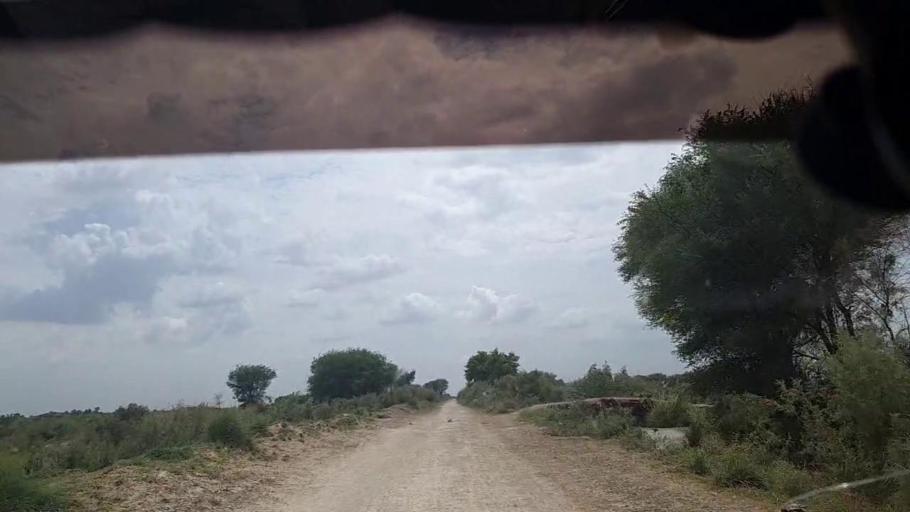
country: PK
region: Sindh
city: Rustam jo Goth
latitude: 28.0369
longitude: 68.9386
